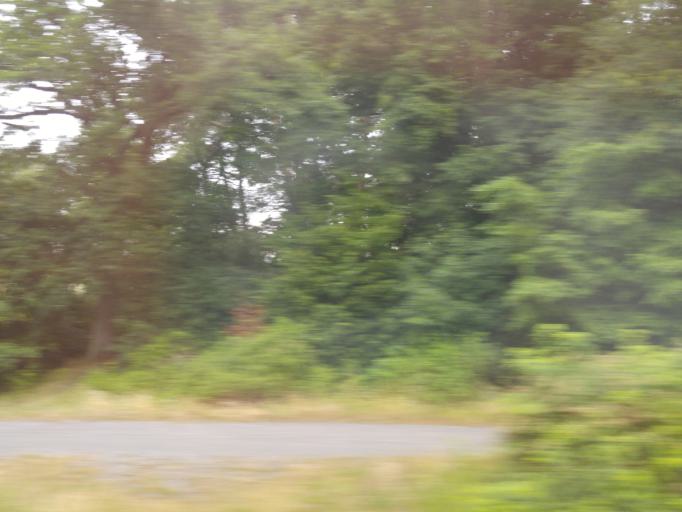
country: DE
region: Hesse
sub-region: Regierungsbezirk Darmstadt
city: Erzhausen
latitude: 49.9545
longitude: 8.6514
